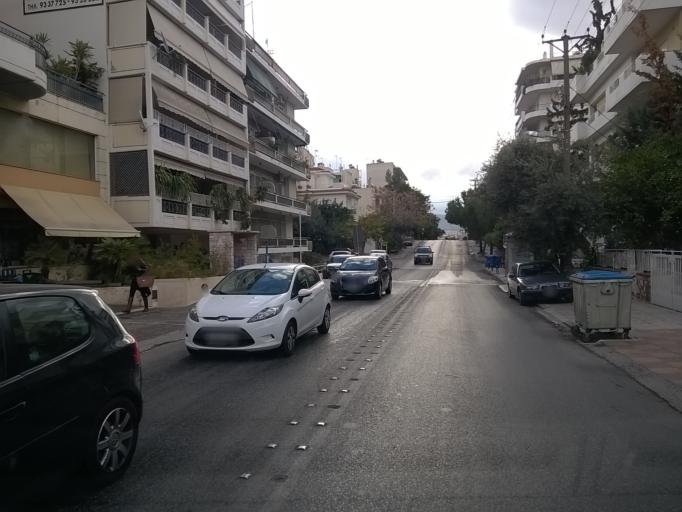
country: GR
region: Attica
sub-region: Nomarchia Athinas
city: Nea Smyrni
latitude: 37.9468
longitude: 23.7238
